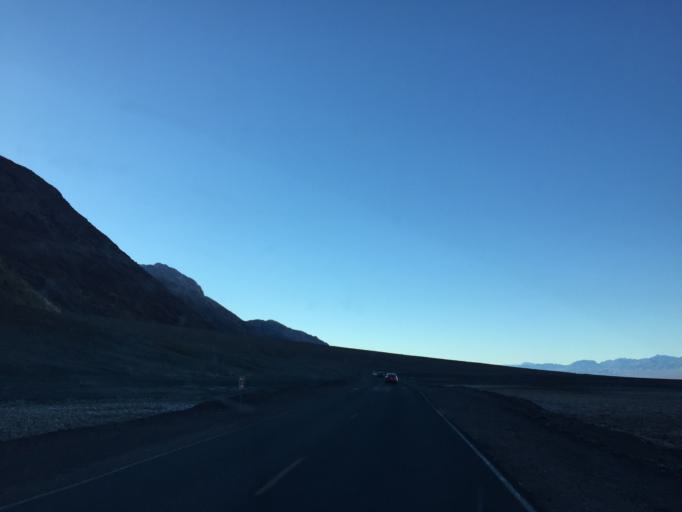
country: US
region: Nevada
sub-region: Nye County
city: Beatty
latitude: 36.2172
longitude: -116.7735
